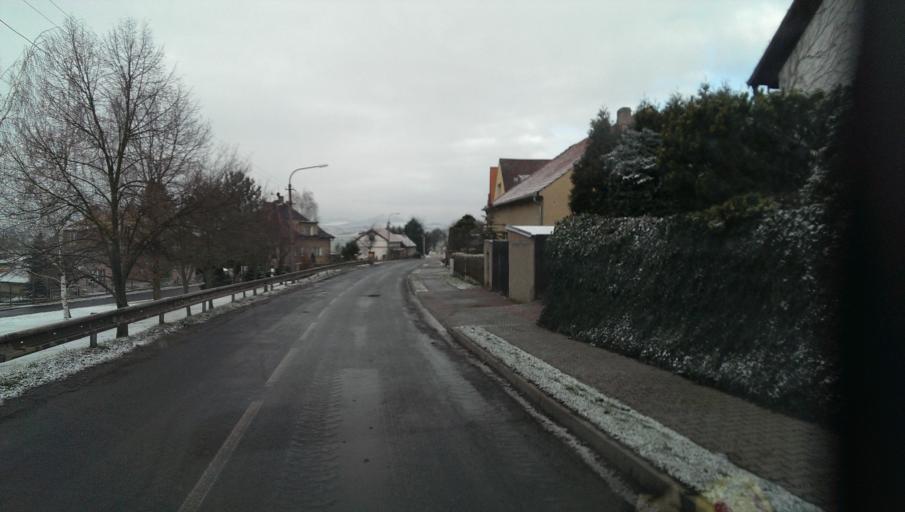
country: CZ
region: Ustecky
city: Trebenice
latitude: 50.4352
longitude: 14.0030
